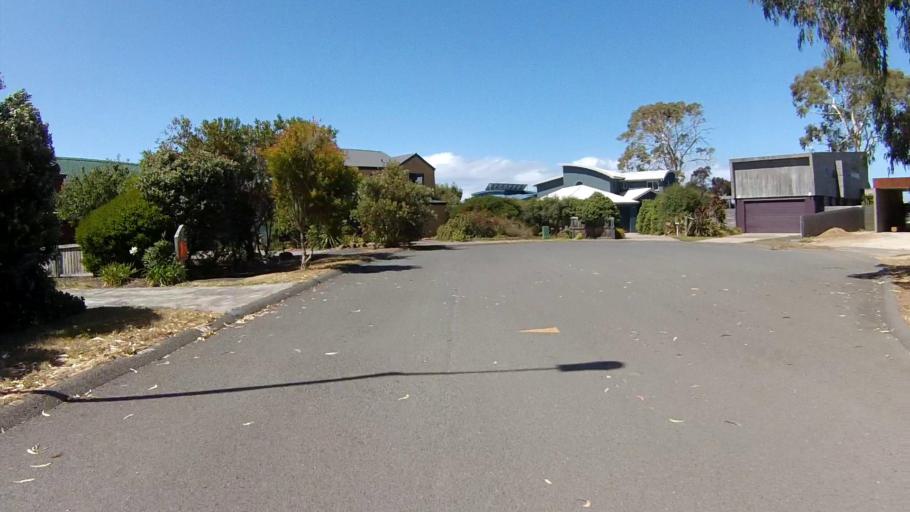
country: AU
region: Tasmania
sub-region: Clarence
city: Acton Park
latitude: -42.8954
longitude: 147.4986
